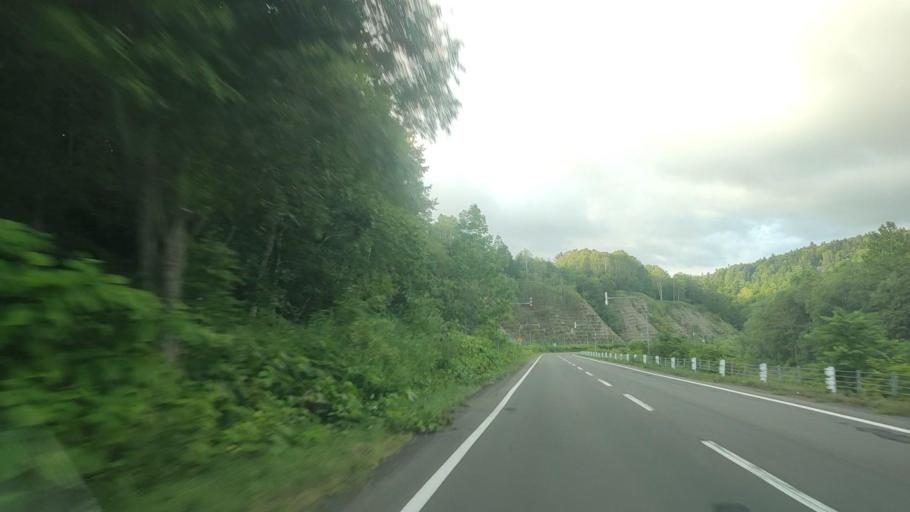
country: JP
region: Hokkaido
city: Bibai
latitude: 43.1180
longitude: 142.0990
